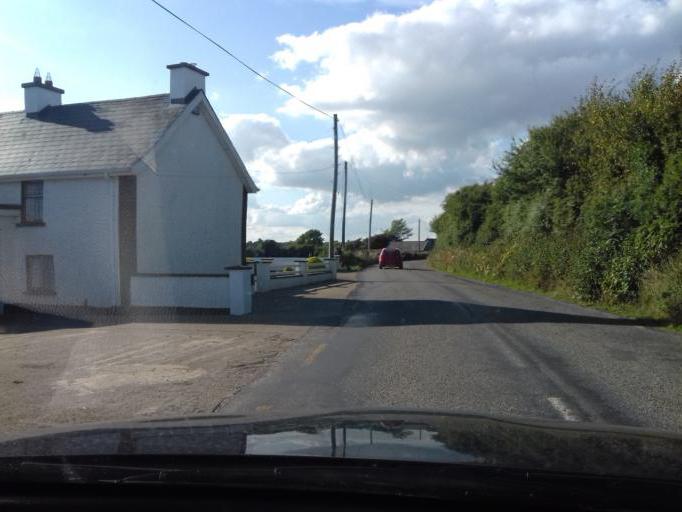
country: IE
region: Munster
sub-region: Waterford
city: Dunmore East
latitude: 52.2485
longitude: -6.8625
